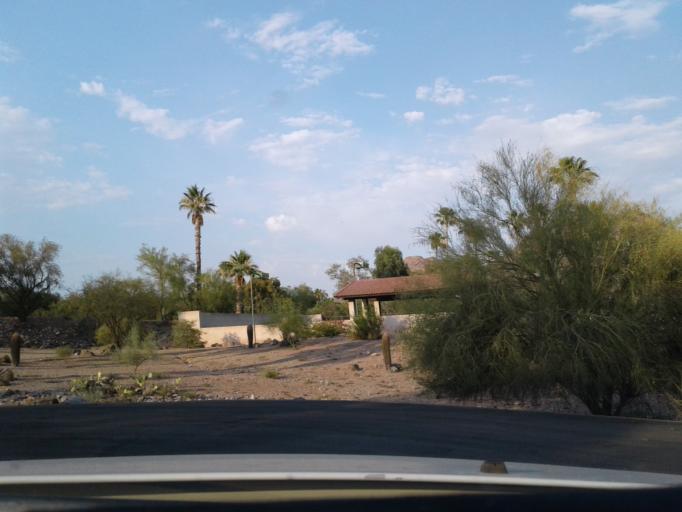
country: US
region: Arizona
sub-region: Maricopa County
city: Paradise Valley
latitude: 33.5421
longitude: -111.9789
